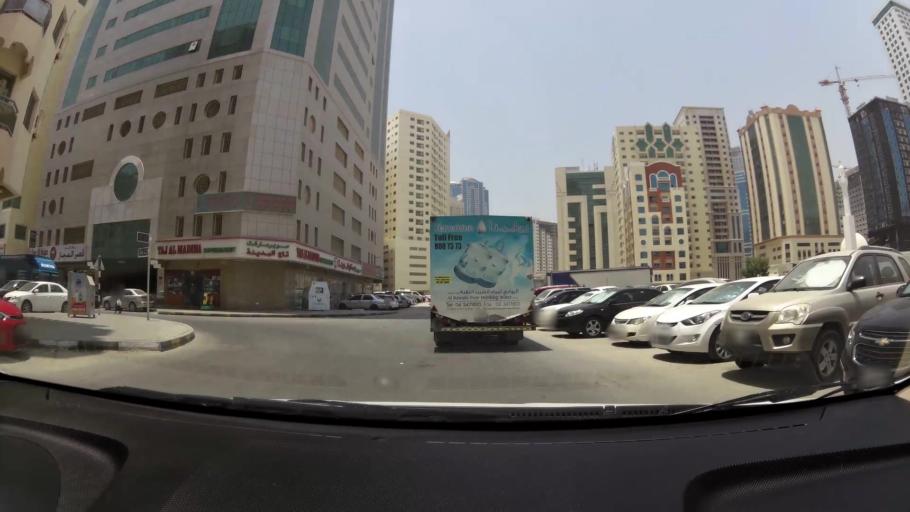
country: AE
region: Ash Shariqah
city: Sharjah
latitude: 25.3189
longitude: 55.3817
